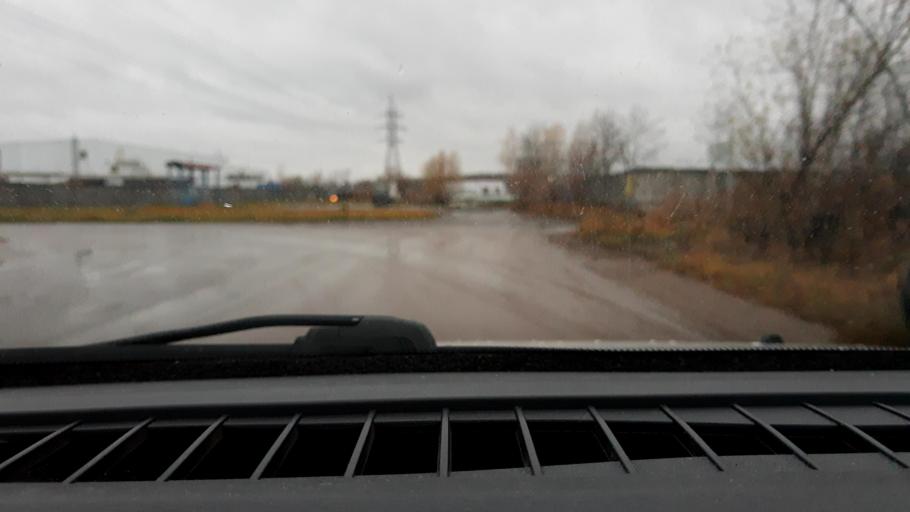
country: RU
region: Nizjnij Novgorod
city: Gorbatovka
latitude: 56.2728
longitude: 43.8516
